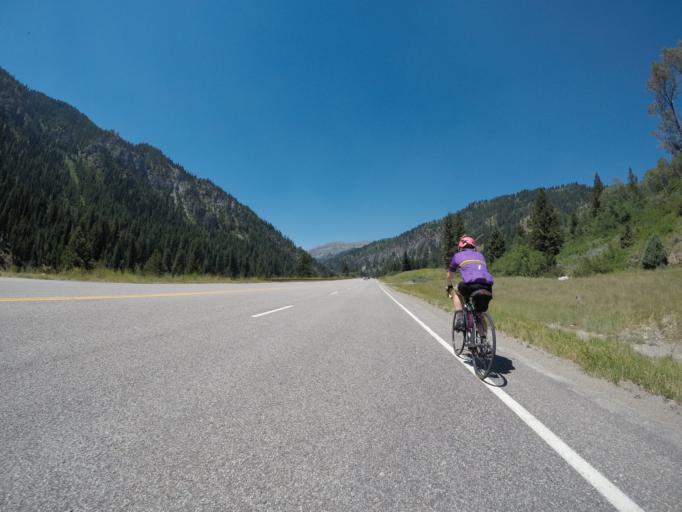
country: US
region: Wyoming
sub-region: Teton County
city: Hoback
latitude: 43.1972
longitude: -110.8907
